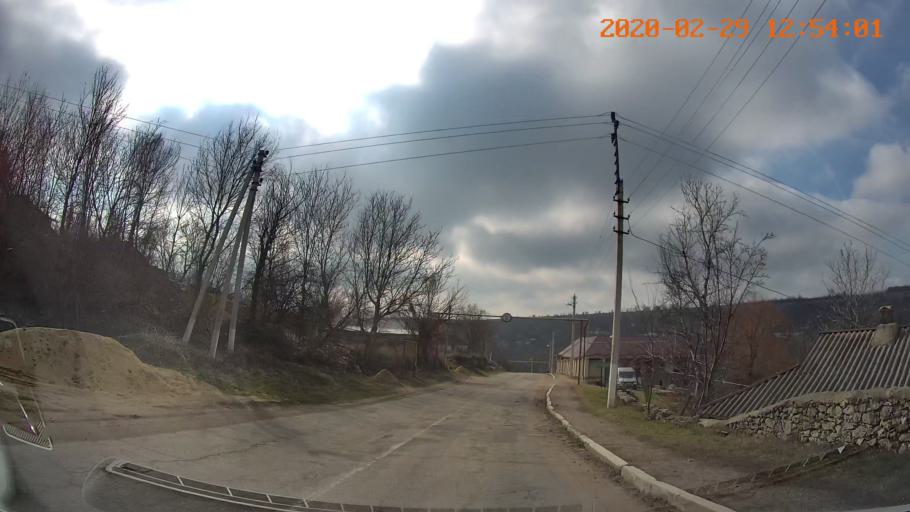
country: MD
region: Telenesti
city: Camenca
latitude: 48.1048
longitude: 28.7298
